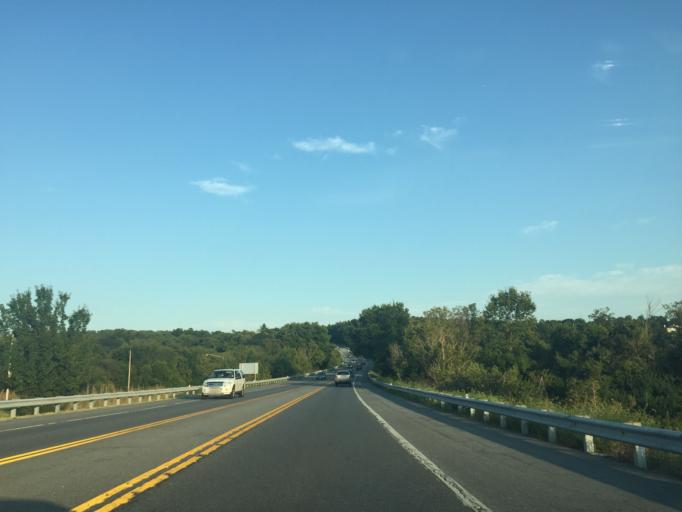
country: US
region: Maryland
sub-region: Frederick County
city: Bartonsville
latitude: 39.4005
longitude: -77.3719
